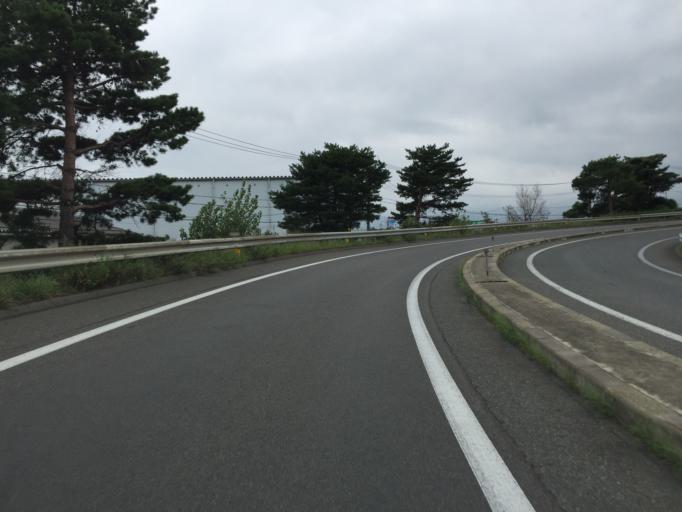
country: JP
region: Fukushima
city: Fukushima-shi
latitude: 37.8022
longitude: 140.4562
